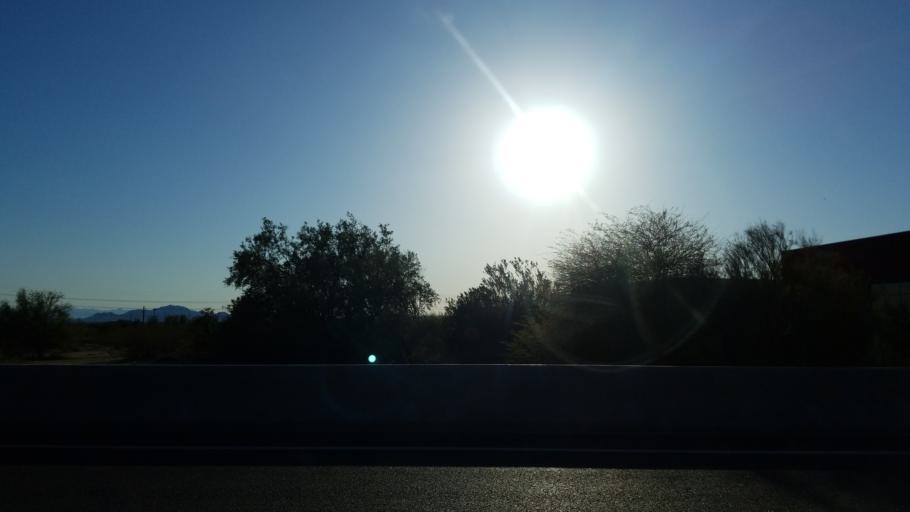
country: US
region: Arizona
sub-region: Maricopa County
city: Paradise Valley
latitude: 33.6573
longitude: -111.8880
